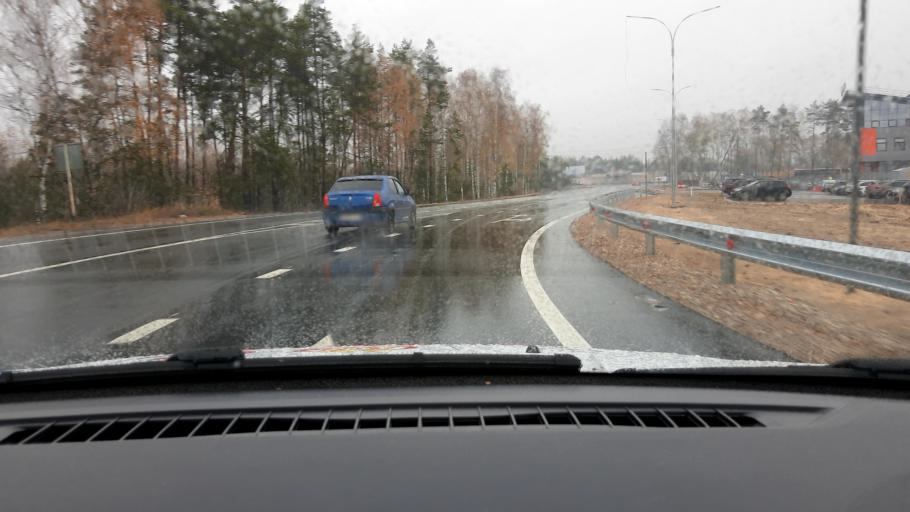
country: RU
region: Nizjnij Novgorod
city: Babino
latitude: 56.3005
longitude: 43.5924
